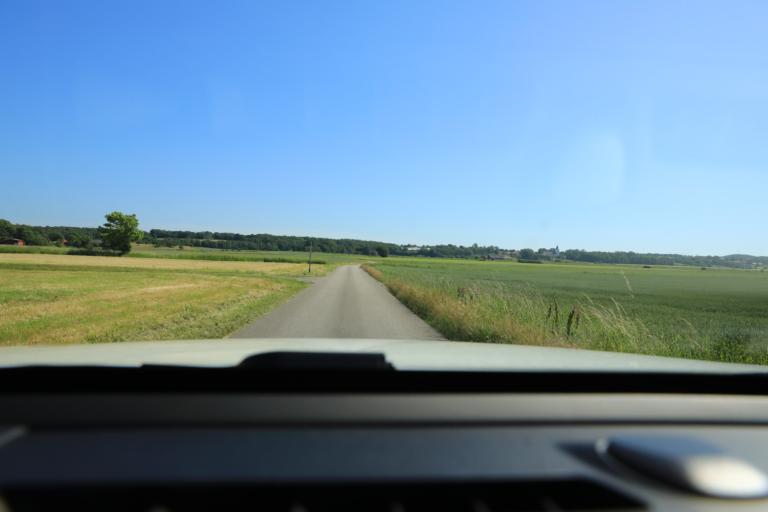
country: SE
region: Halland
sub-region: Varbergs Kommun
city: Varberg
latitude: 57.1727
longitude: 12.3164
